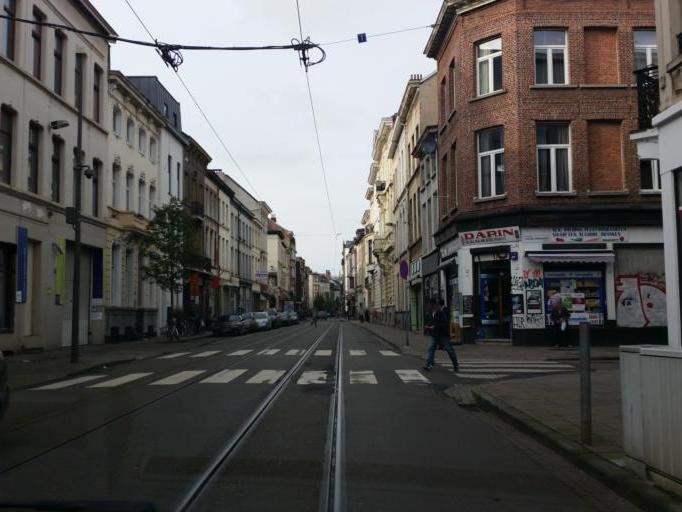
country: BE
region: Flanders
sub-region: Provincie Antwerpen
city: Antwerpen
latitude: 51.2078
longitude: 4.4133
